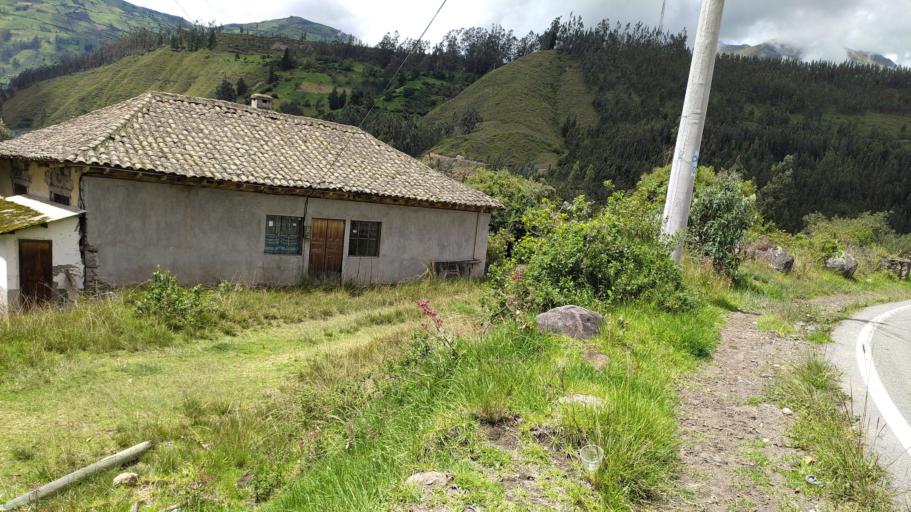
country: EC
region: Chimborazo
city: Guano
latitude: -1.6491
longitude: -78.5833
